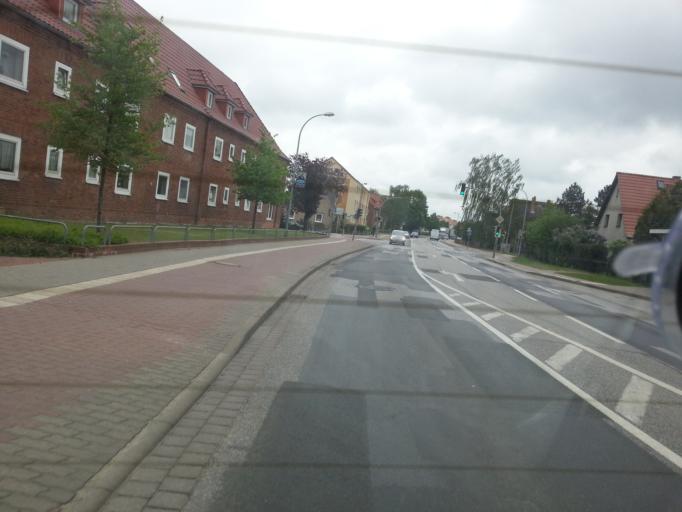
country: DE
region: Mecklenburg-Vorpommern
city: Waren
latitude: 53.5206
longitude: 12.6686
